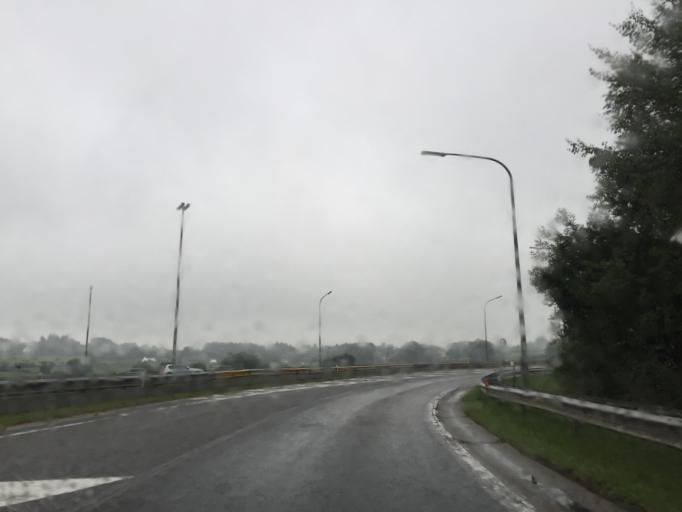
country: BE
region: Wallonia
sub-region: Province de Liege
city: Jalhay
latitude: 50.5291
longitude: 5.9171
